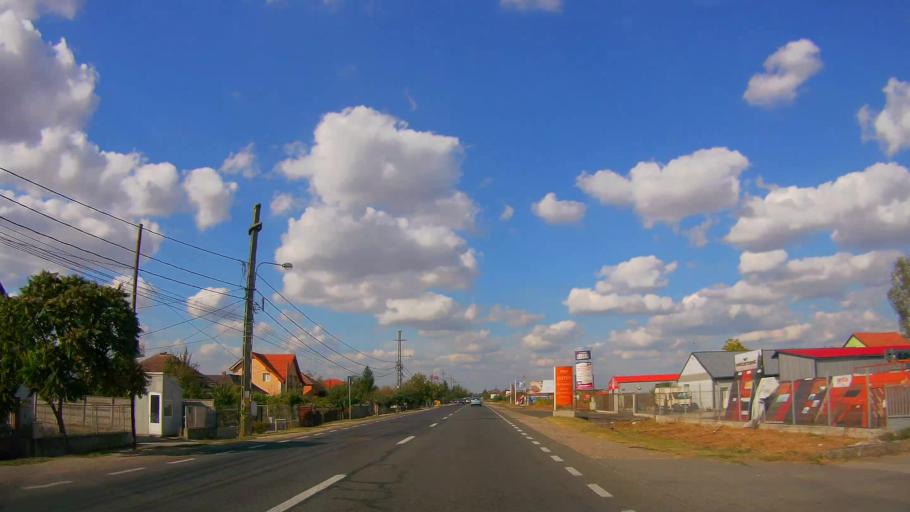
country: RO
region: Satu Mare
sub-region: Comuna Paulesti
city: Paulesti
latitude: 47.7558
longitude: 22.8832
